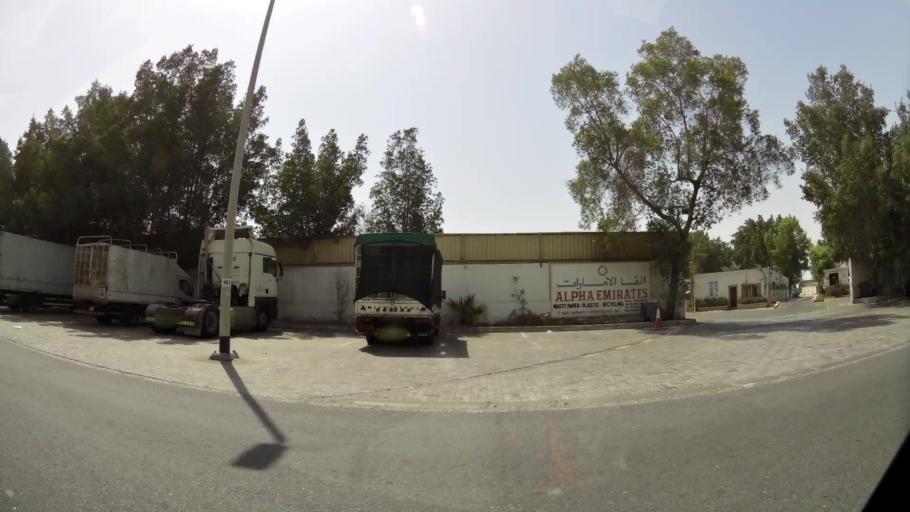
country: AE
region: Dubai
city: Dubai
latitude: 25.1450
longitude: 55.2386
